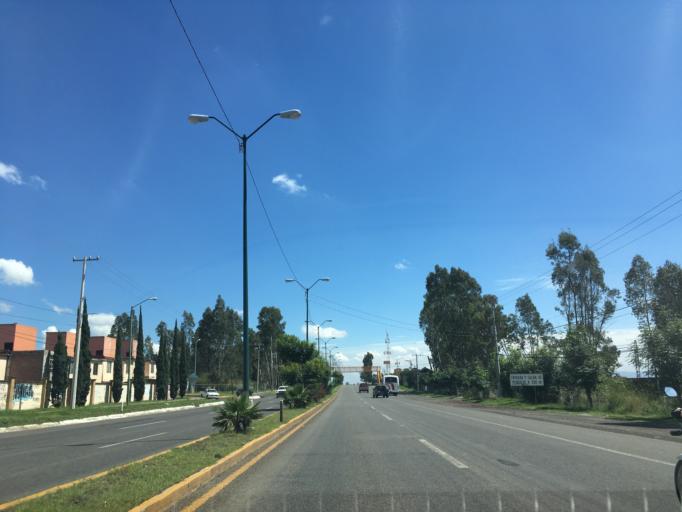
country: MX
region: Michoacan
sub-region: Morelia
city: Lomas de la Maestranza
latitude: 19.6845
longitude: -101.3308
